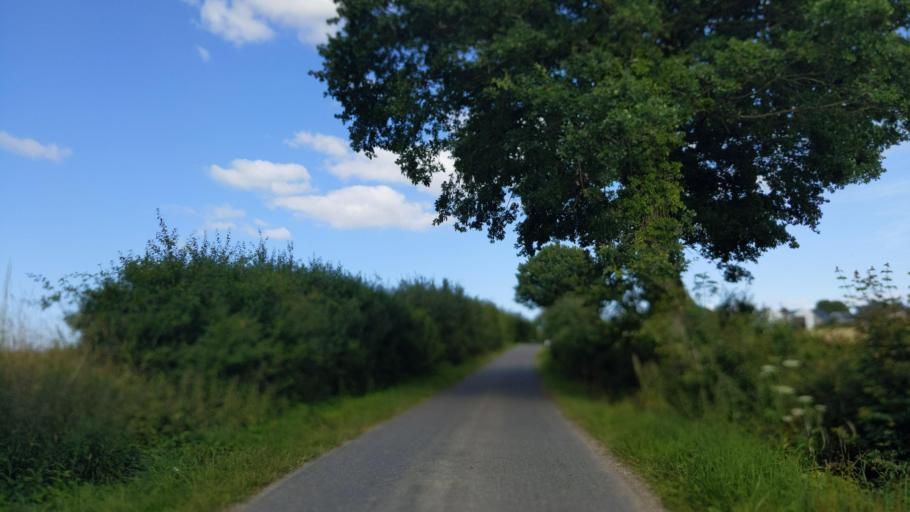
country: DE
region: Schleswig-Holstein
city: Stockelsdorf
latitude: 53.9414
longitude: 10.6494
